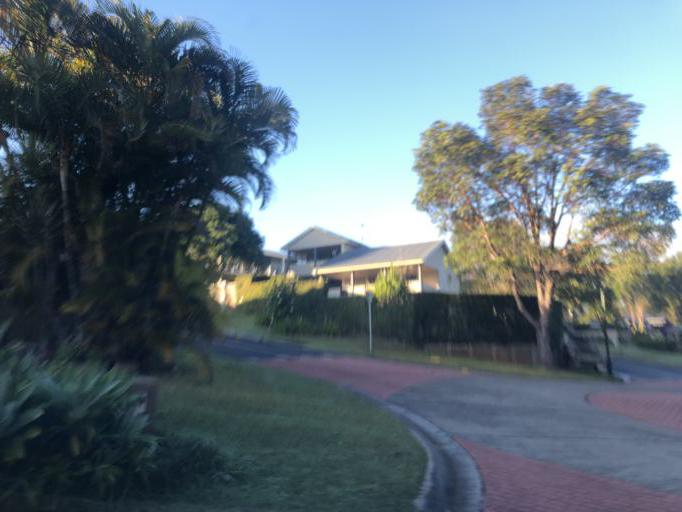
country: AU
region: New South Wales
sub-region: Coffs Harbour
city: Coffs Harbour
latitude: -30.2938
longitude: 153.1293
